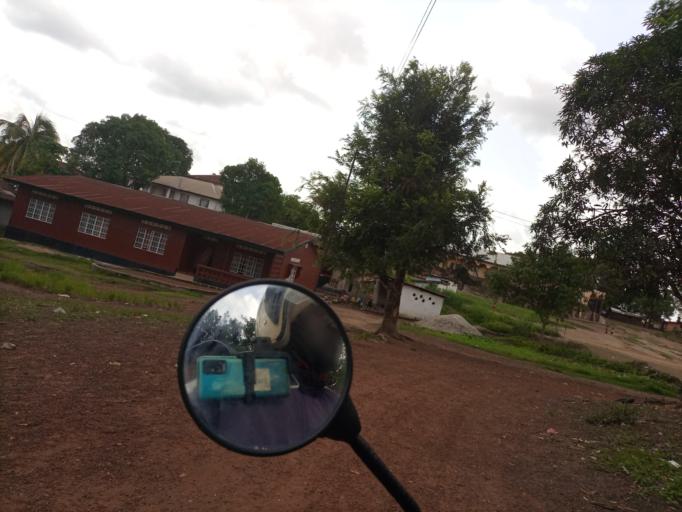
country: SL
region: Southern Province
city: Bo
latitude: 7.9494
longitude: -11.7333
